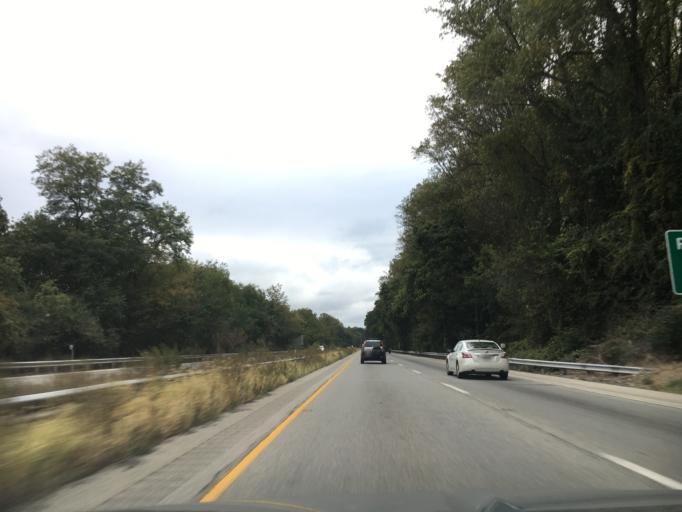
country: US
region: Pennsylvania
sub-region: Chester County
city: Caln
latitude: 40.0055
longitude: -75.7662
